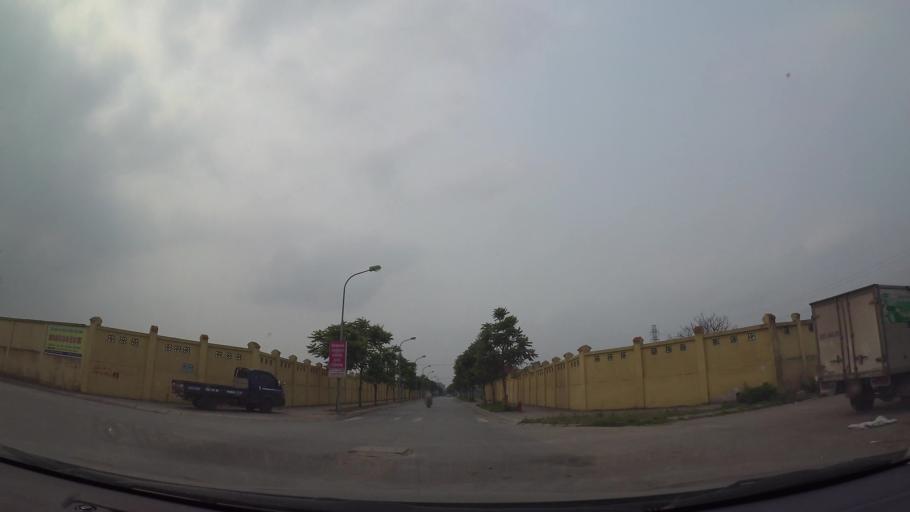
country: VN
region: Ha Noi
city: Trau Quy
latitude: 21.0555
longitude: 105.9035
